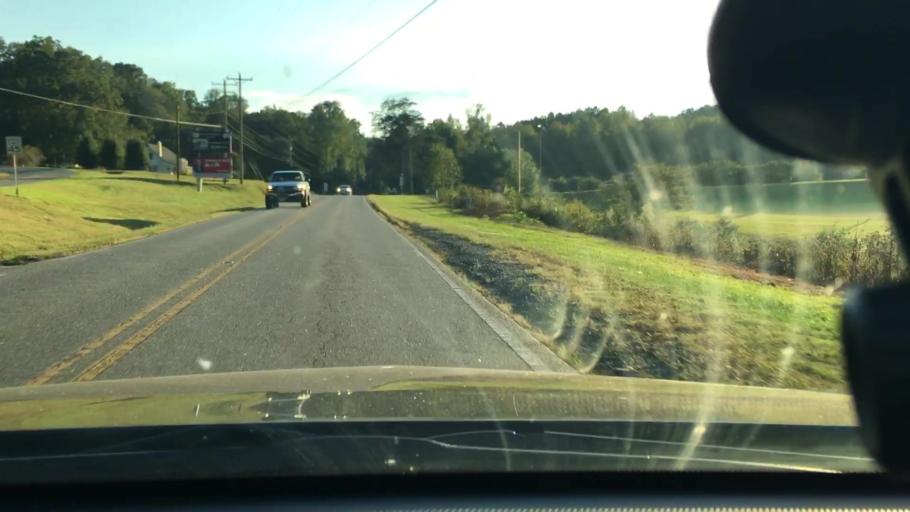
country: US
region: North Carolina
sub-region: Polk County
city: Columbus
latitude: 35.2947
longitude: -82.1656
